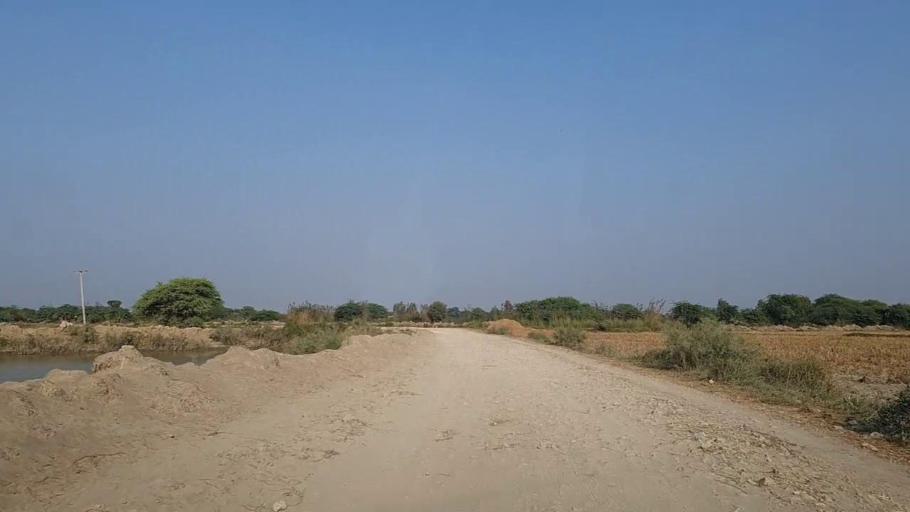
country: PK
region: Sindh
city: Mirpur Sakro
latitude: 24.6228
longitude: 67.7444
